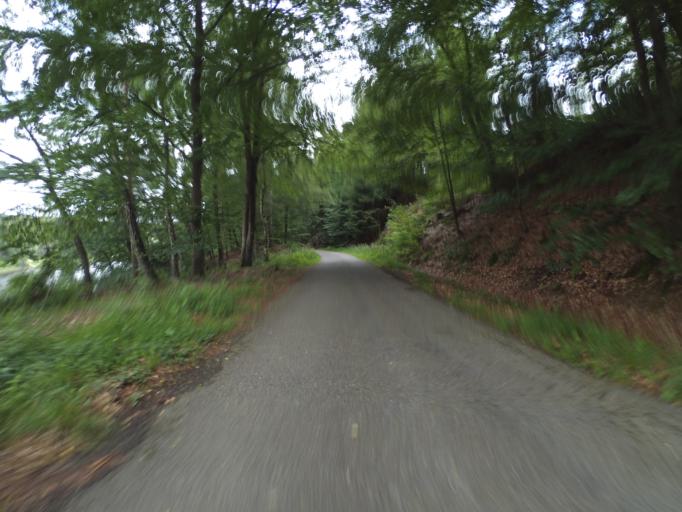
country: BE
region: Wallonia
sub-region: Province de Liege
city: Eupen
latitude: 50.6089
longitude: 6.0939
